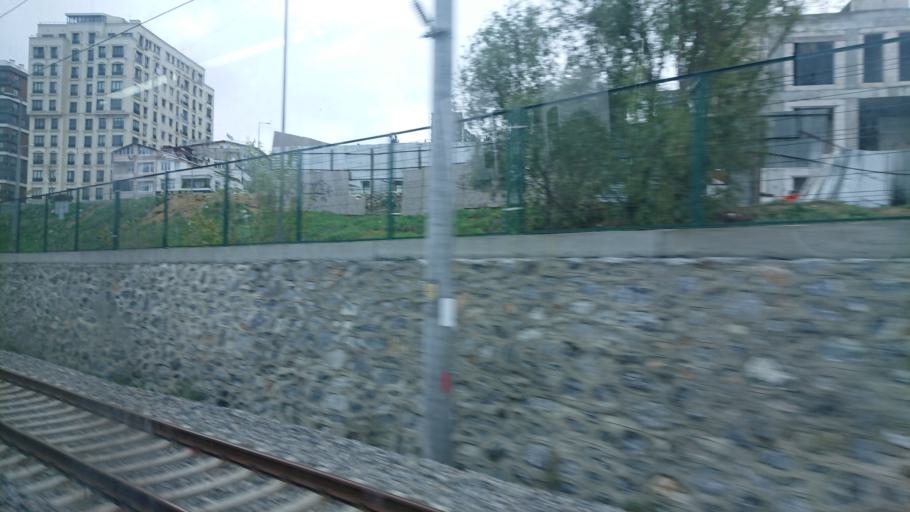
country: TR
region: Istanbul
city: Mahmutbey
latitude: 41.0038
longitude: 28.7720
